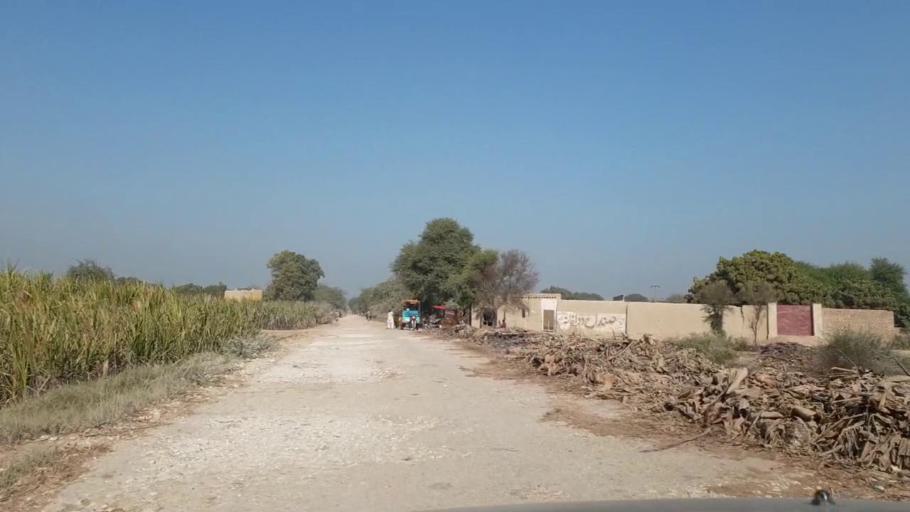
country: PK
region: Sindh
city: Tando Allahyar
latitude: 25.5699
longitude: 68.6079
